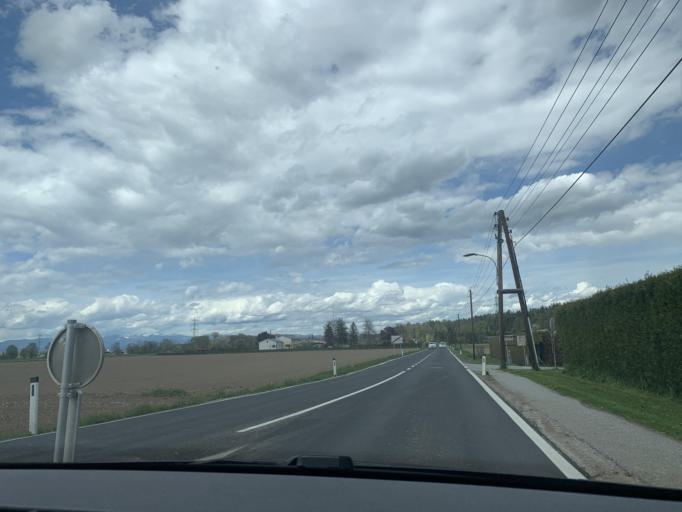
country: AT
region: Styria
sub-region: Politischer Bezirk Graz-Umgebung
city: Zettling
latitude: 46.9317
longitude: 15.3891
